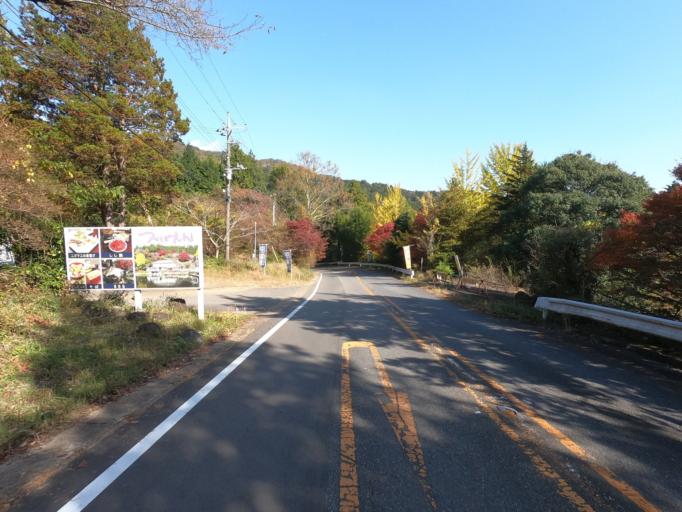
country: JP
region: Ibaraki
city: Makabe
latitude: 36.2352
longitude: 140.1285
